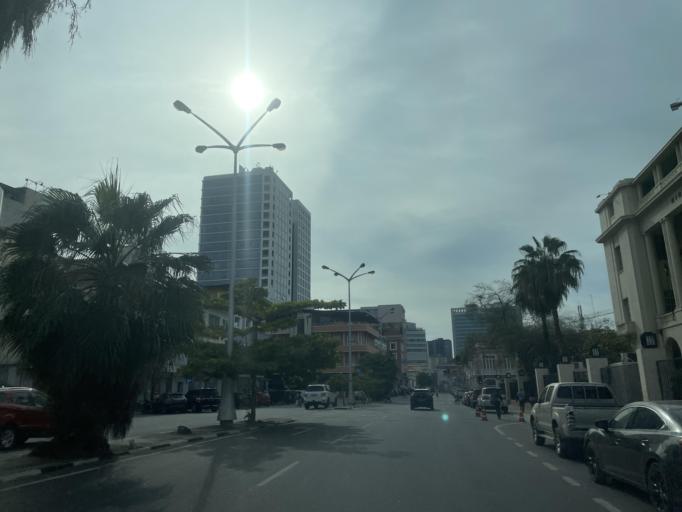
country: AO
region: Luanda
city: Luanda
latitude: -8.8131
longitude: 13.2341
